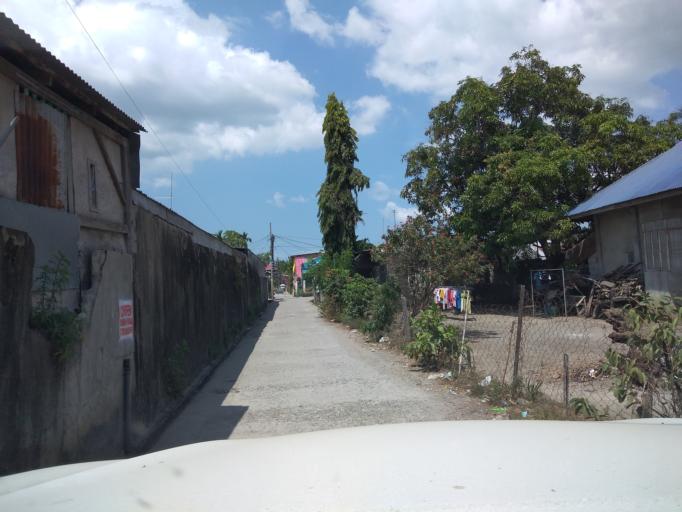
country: PH
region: Central Luzon
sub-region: Province of Pampanga
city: Bahay Pare
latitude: 15.0164
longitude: 120.8745
